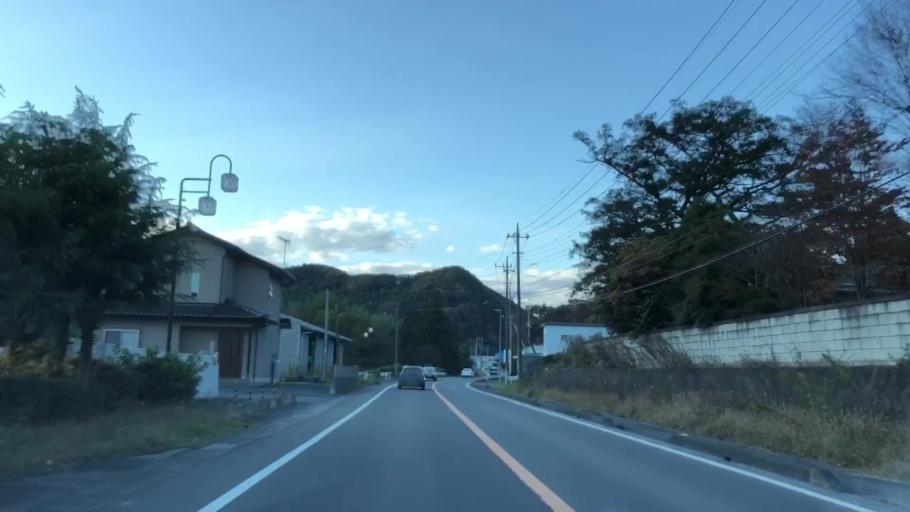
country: JP
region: Ibaraki
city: Kasama
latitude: 36.4821
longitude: 140.2926
